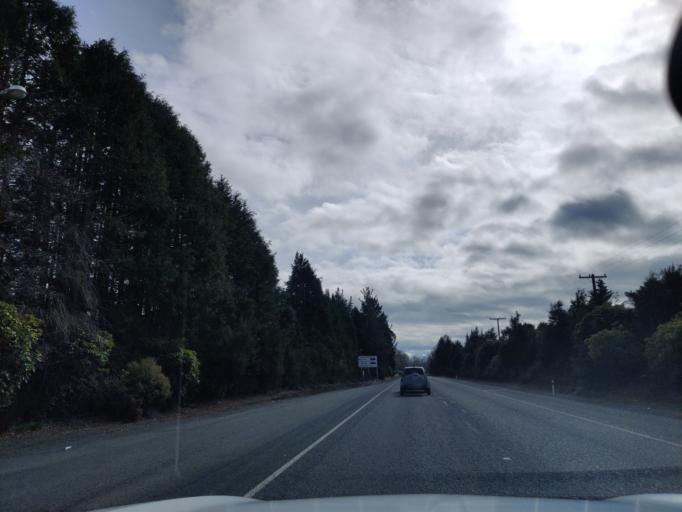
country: NZ
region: Waikato
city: Turangi
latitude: -39.0068
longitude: 175.8055
